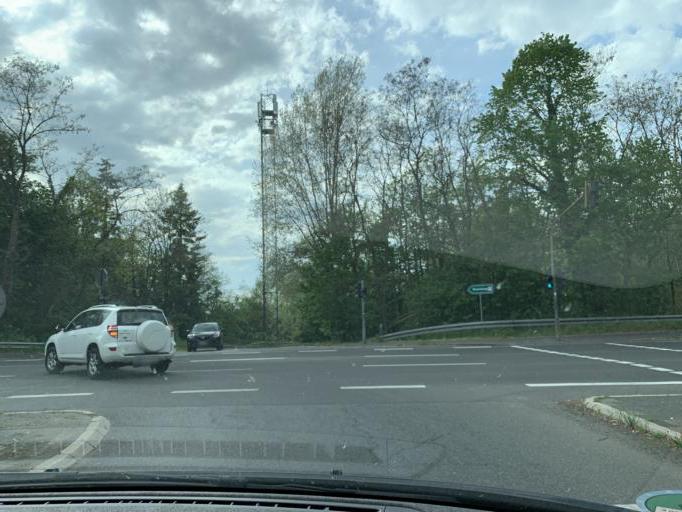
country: DE
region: North Rhine-Westphalia
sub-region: Regierungsbezirk Koln
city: Hurth
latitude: 50.8391
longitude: 6.8689
